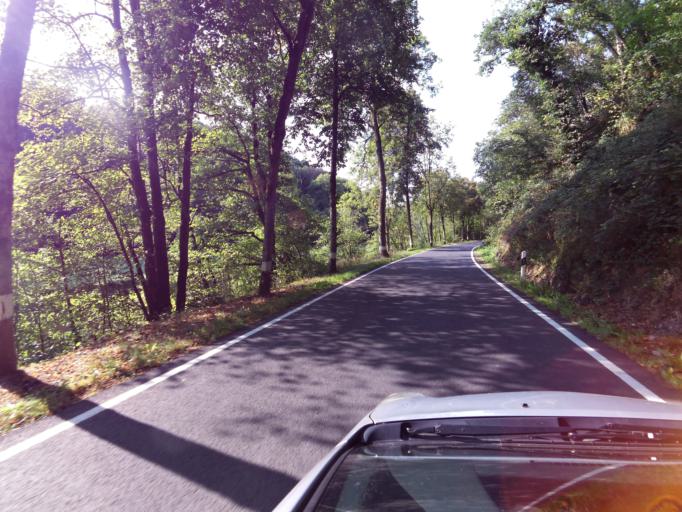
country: LU
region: Diekirch
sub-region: Canton de Wiltz
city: Goesdorf
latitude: 49.9236
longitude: 6.0038
